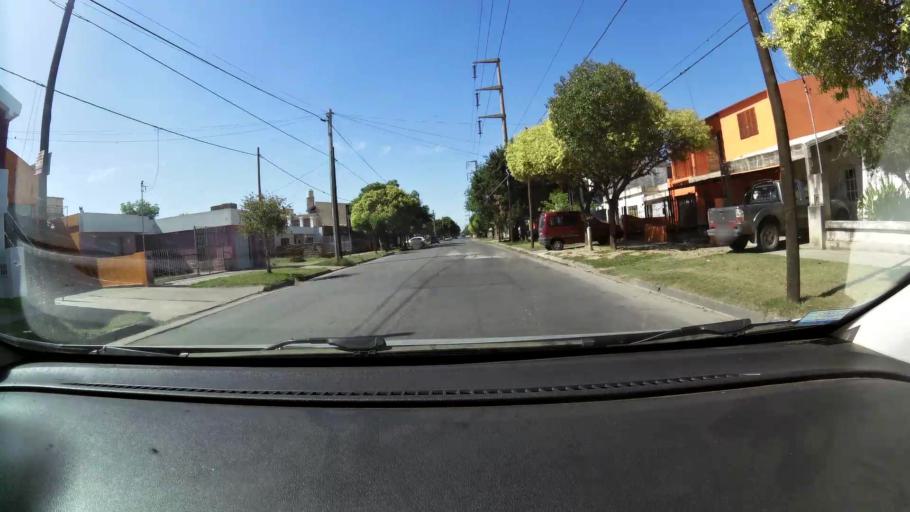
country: AR
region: Cordoba
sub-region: Departamento de Capital
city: Cordoba
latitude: -31.3761
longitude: -64.1676
